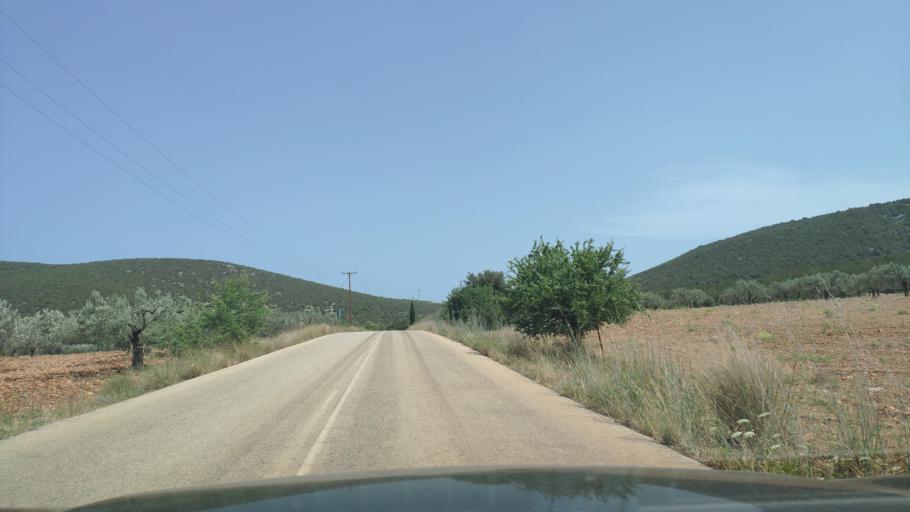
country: GR
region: Peloponnese
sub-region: Nomos Argolidos
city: Didyma
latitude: 37.4513
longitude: 23.1763
